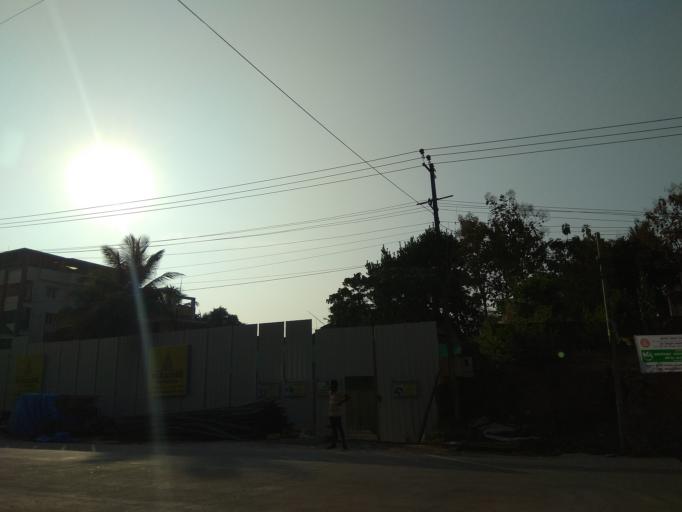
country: IN
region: Karnataka
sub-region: Dakshina Kannada
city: Mangalore
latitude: 12.9028
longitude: 74.8456
